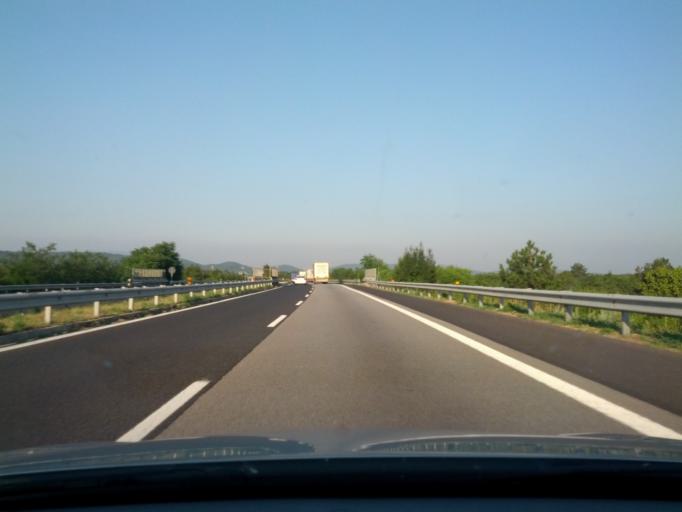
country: IT
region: Friuli Venezia Giulia
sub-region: Provincia di Trieste
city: Villa Opicina
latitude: 45.7001
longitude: 13.7730
